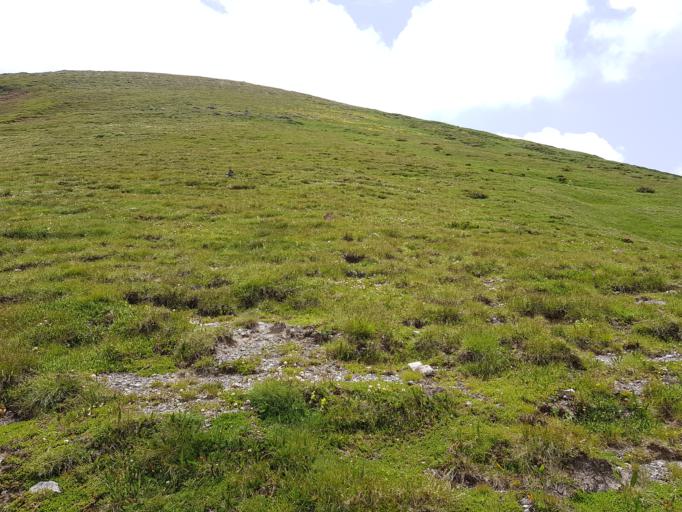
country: IT
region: Piedmont
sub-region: Provincia di Cuneo
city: Frabosa Soprana
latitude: 44.1881
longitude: 7.7752
